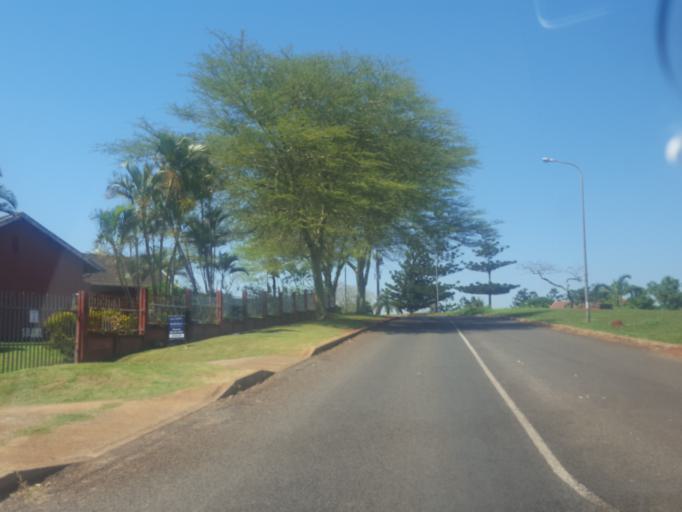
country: ZA
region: KwaZulu-Natal
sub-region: uThungulu District Municipality
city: Empangeni
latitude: -28.7588
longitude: 31.9025
